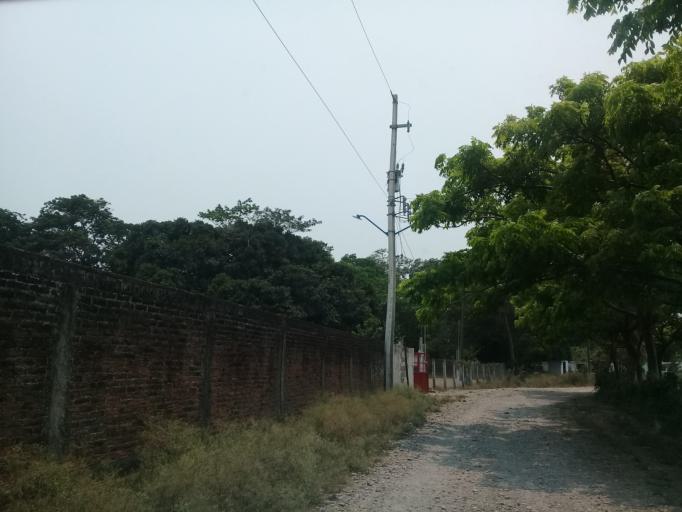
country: MX
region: Veracruz
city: Jamapa
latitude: 18.9317
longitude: -96.2104
